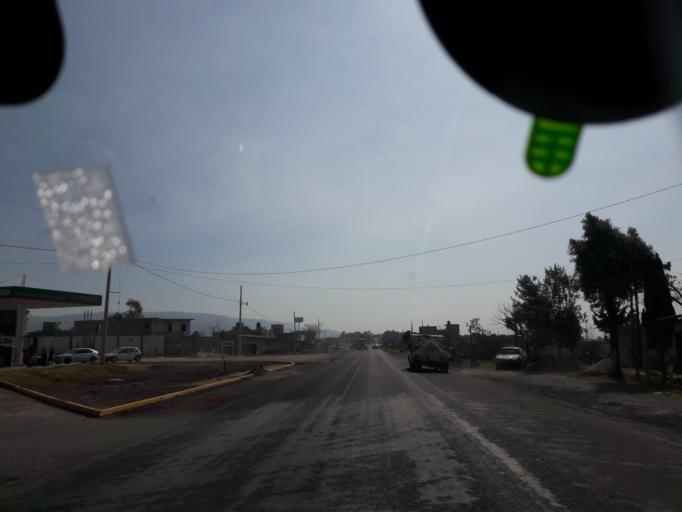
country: MX
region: Tlaxcala
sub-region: Ixtacuixtla de Mariano Matamoros
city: Santa Justina Ecatepec
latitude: 19.3131
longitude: -98.3377
